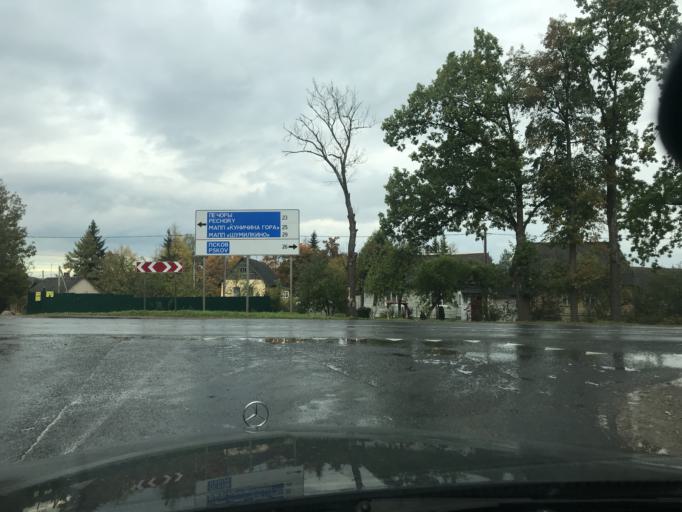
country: RU
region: Pskov
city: Izborsk
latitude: 57.7048
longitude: 27.8722
